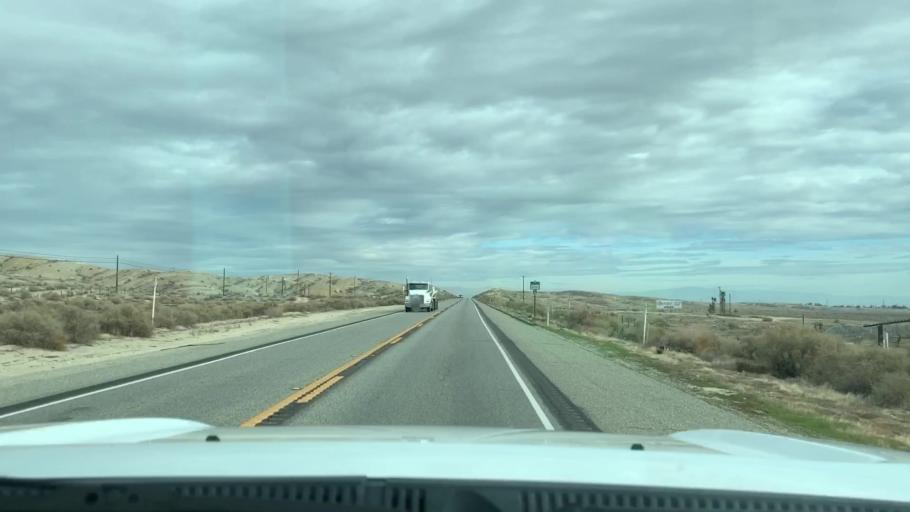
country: US
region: California
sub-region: Kern County
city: Ford City
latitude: 35.2328
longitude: -119.3703
